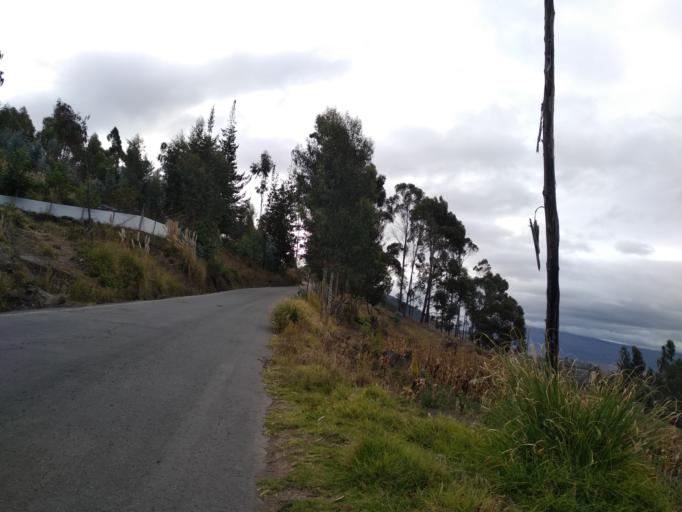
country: EC
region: Chimborazo
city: Riobamba
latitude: -1.7059
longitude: -78.6960
